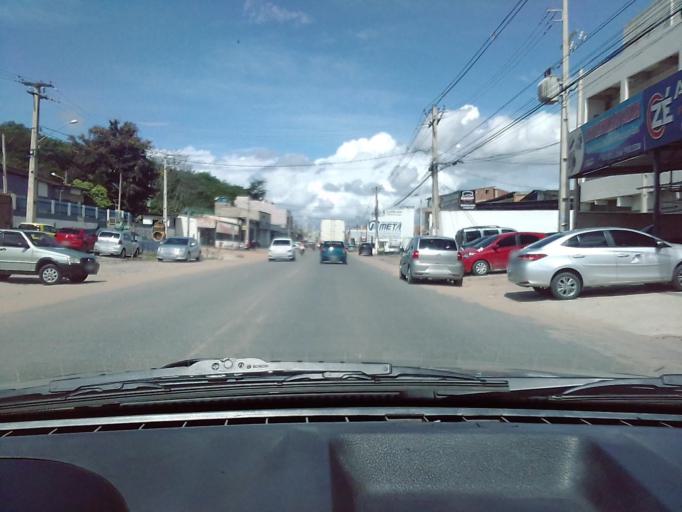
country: BR
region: Pernambuco
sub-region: Vitoria De Santo Antao
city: Vitoria de Santo Antao
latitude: -8.1177
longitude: -35.3028
